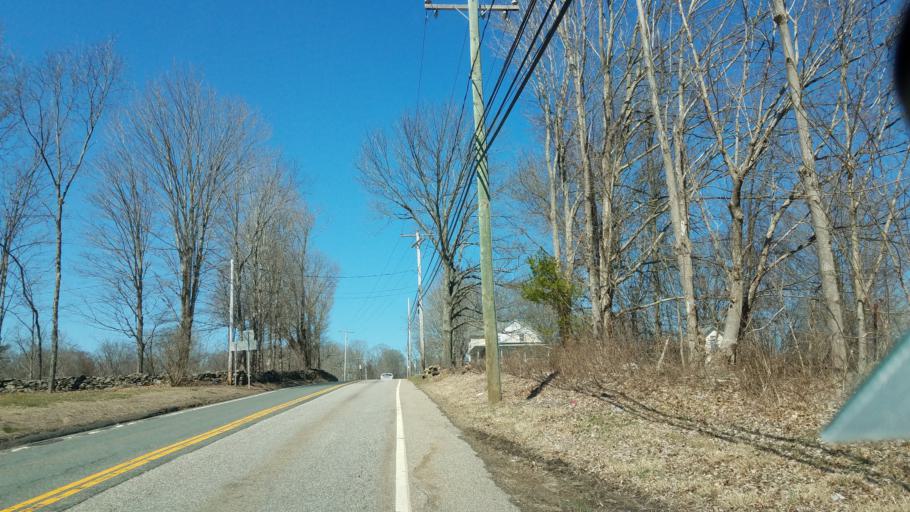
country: US
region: Connecticut
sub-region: Tolland County
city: South Coventry
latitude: 41.8023
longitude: -72.3015
